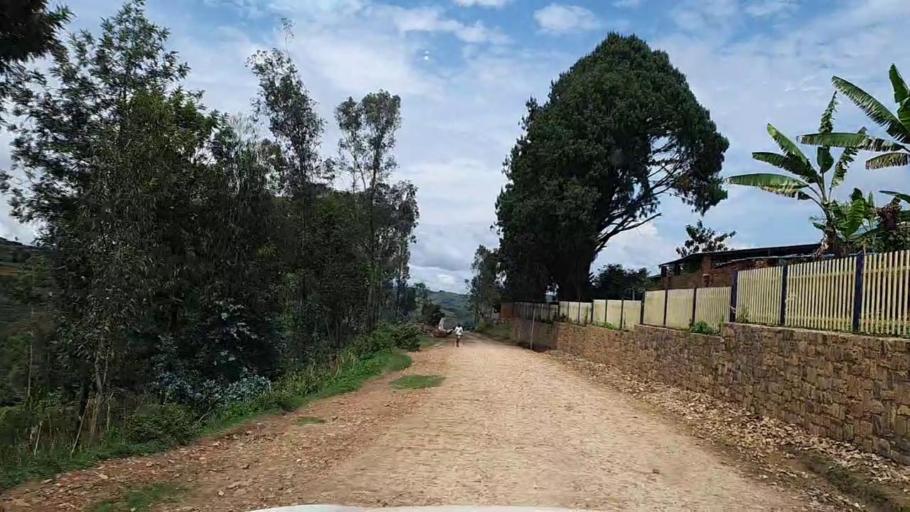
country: RW
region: Southern Province
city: Gikongoro
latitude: -2.3343
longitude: 29.5233
